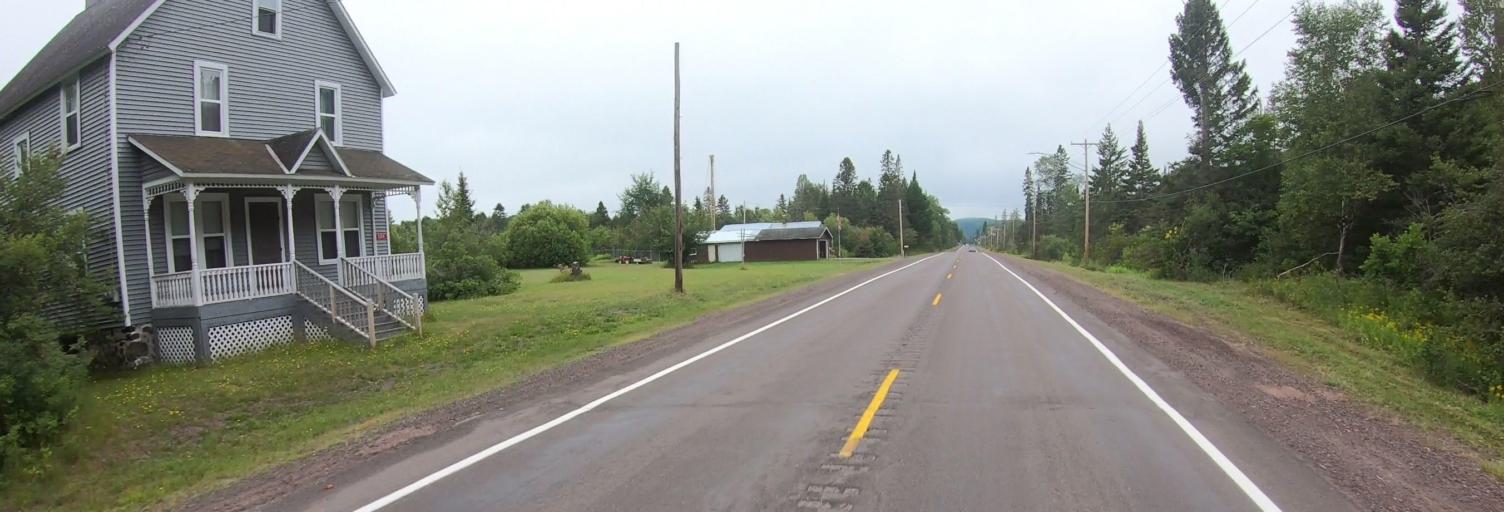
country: US
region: Michigan
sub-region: Keweenaw County
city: Eagle River
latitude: 47.3866
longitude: -88.2873
